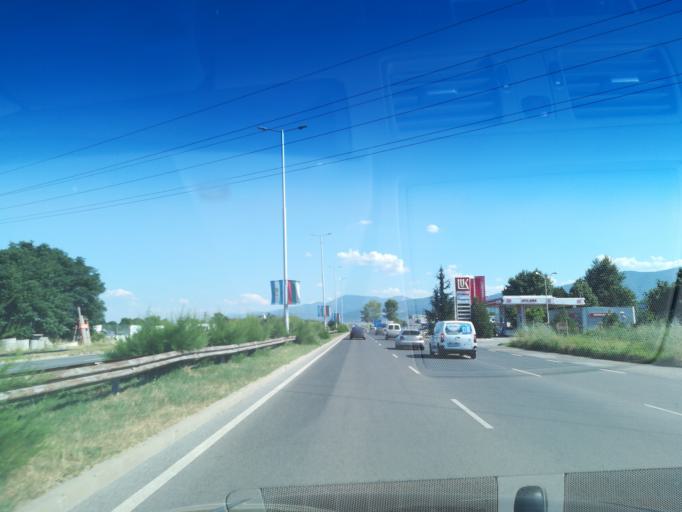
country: BG
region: Plovdiv
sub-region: Obshtina Plovdiv
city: Plovdiv
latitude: 42.1032
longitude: 24.7855
